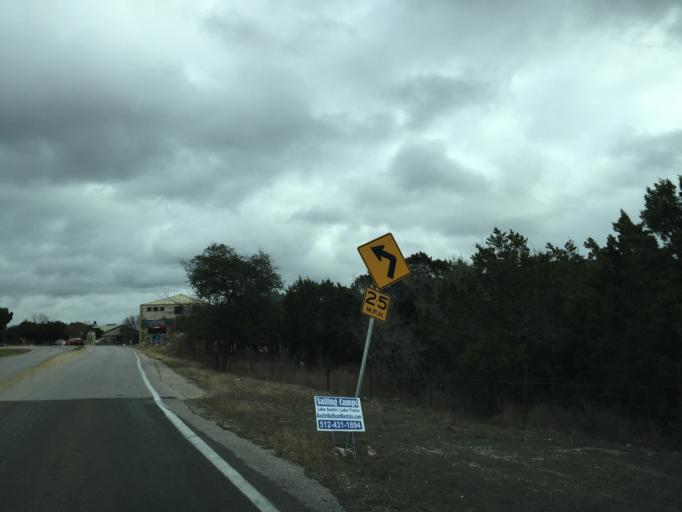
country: US
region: Texas
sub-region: Travis County
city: Hudson Bend
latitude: 30.4027
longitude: -97.8715
